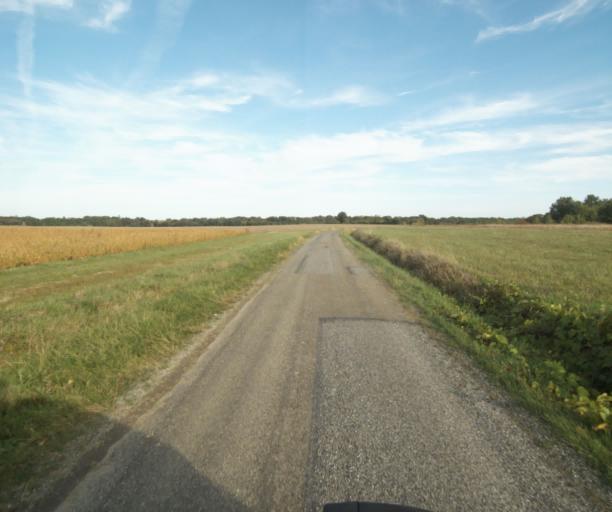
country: FR
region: Midi-Pyrenees
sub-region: Departement du Tarn-et-Garonne
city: Finhan
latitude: 43.9050
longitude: 1.1314
